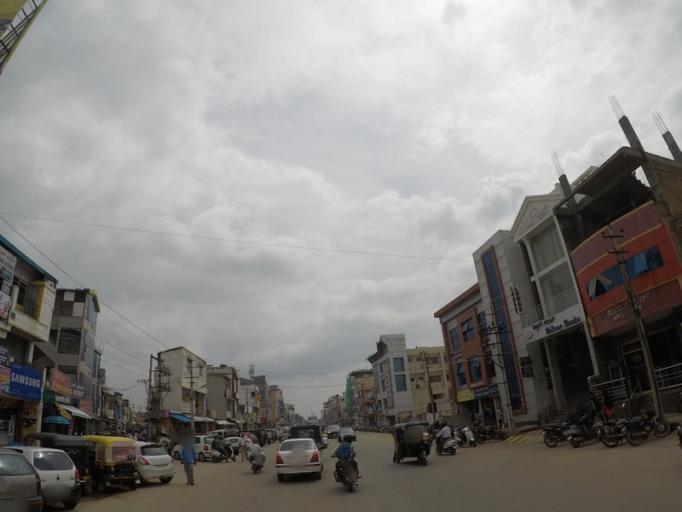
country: IN
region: Karnataka
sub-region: Chikmagalur
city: Chikmagalur
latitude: 13.3231
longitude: 75.7721
